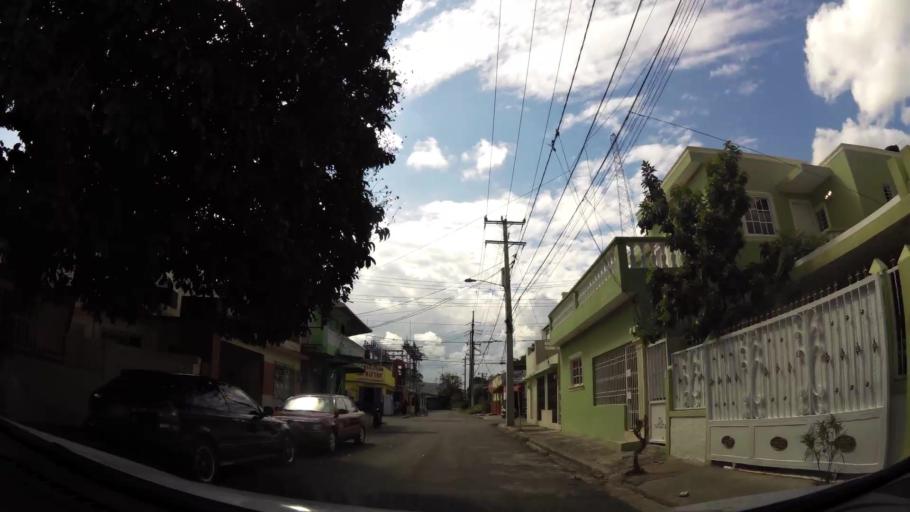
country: DO
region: La Vega
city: Concepcion de La Vega
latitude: 19.2239
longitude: -70.5345
